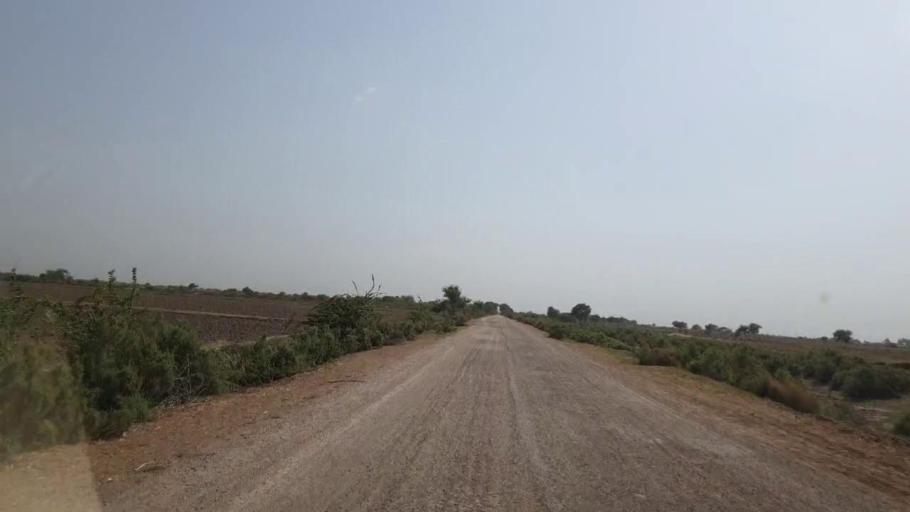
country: PK
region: Sindh
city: Rajo Khanani
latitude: 25.0362
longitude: 68.8730
